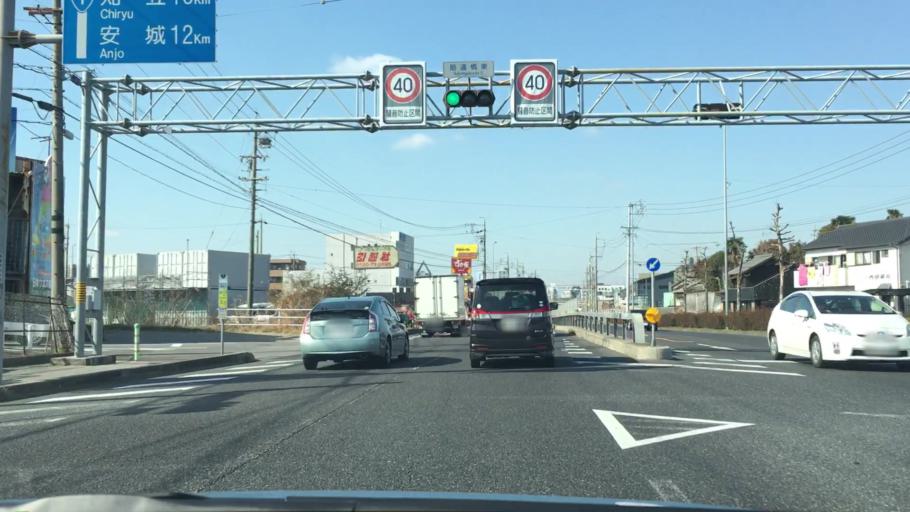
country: JP
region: Aichi
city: Okazaki
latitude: 34.9483
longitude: 137.1846
